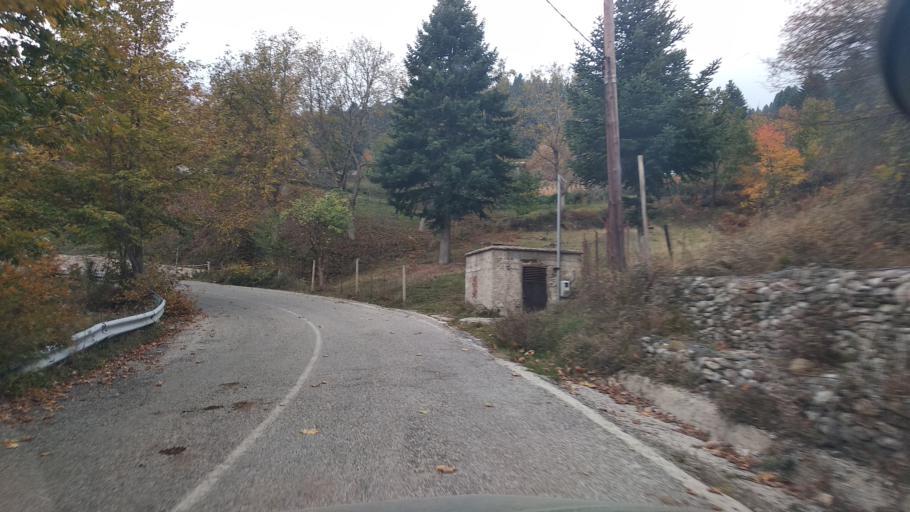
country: GR
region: Thessaly
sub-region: Trikala
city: Kalampaka
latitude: 39.5889
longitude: 21.4903
